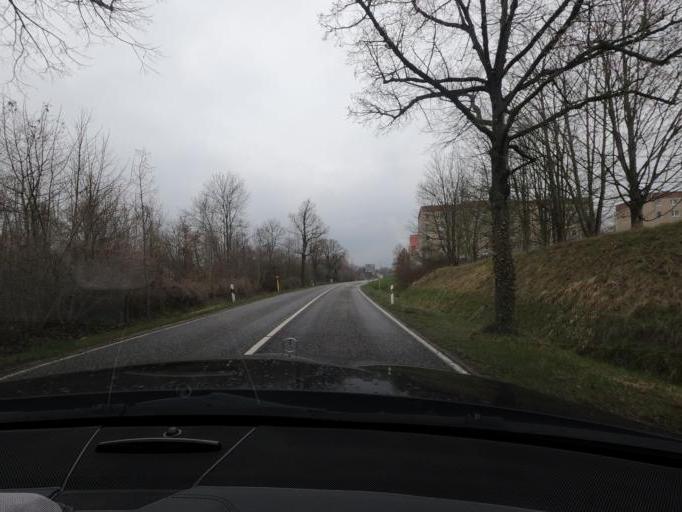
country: DE
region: Thuringia
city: Muehlhausen
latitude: 51.2199
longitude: 10.4057
